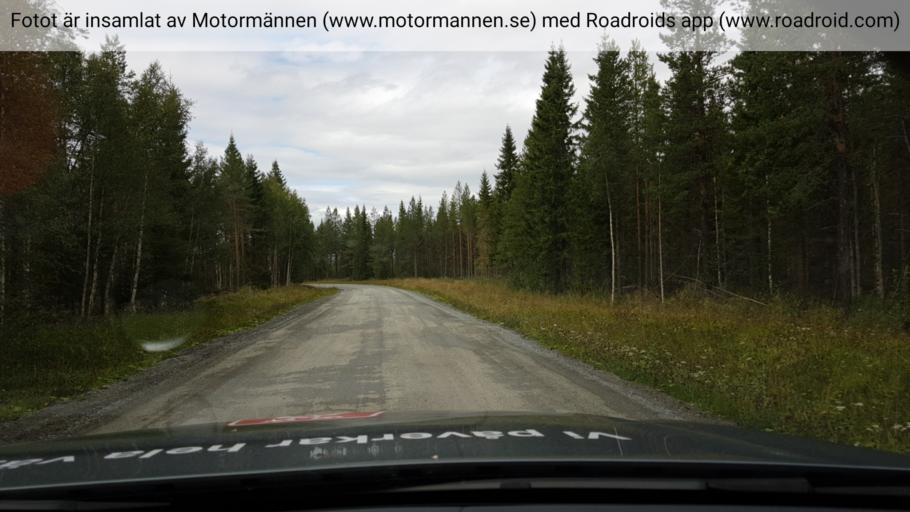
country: SE
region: Jaemtland
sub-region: Krokoms Kommun
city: Valla
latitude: 63.6554
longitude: 13.7770
